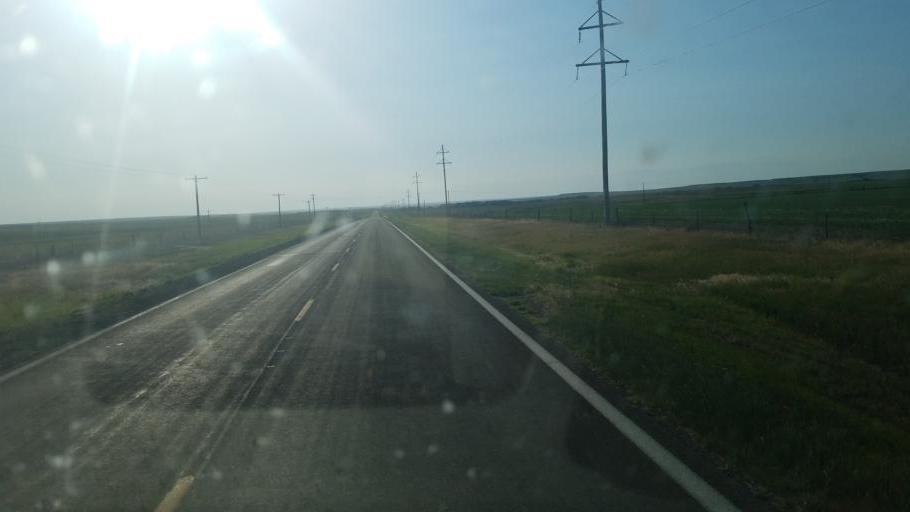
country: US
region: Kansas
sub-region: Hodgeman County
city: Jetmore
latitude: 38.0880
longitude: -99.8656
